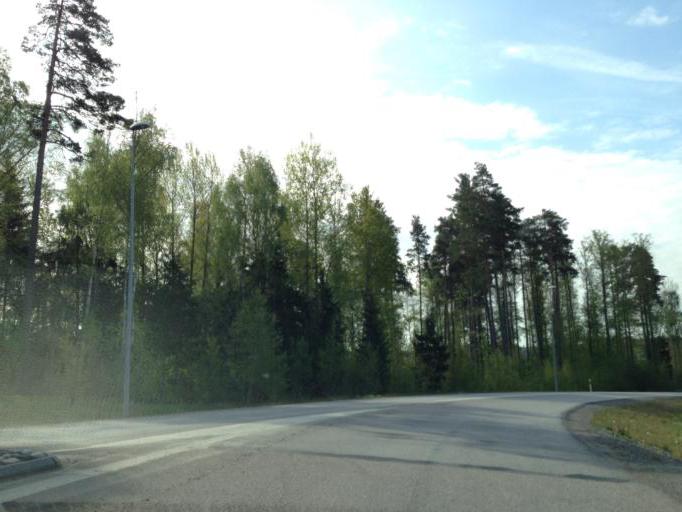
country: SE
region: Soedermanland
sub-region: Flens Kommun
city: Malmkoping
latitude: 59.1389
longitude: 16.7132
